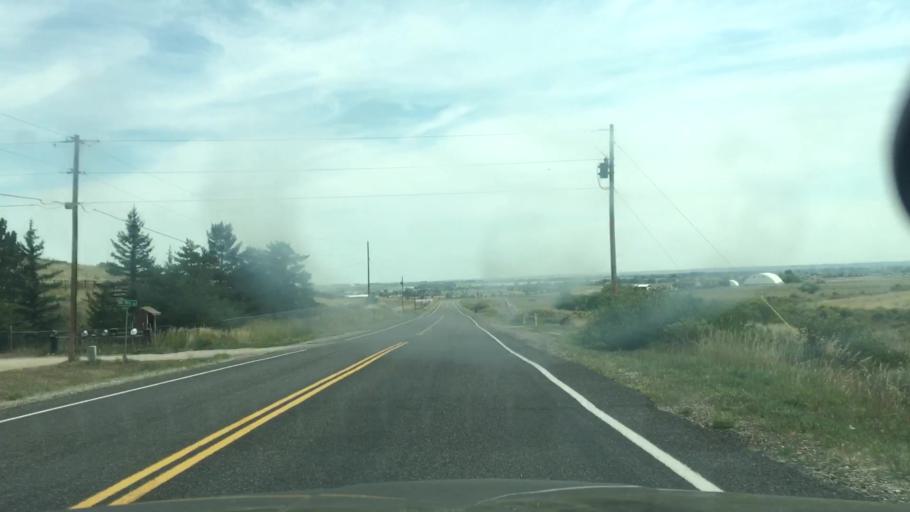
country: US
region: Colorado
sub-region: Larimer County
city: Campion
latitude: 40.3374
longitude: -105.1770
